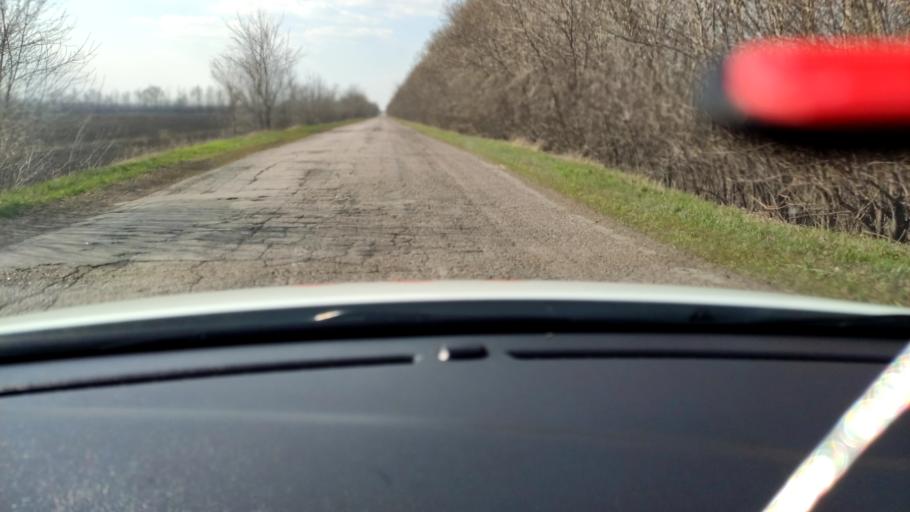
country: RU
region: Voronezj
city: Uryv-Pokrovka
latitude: 51.1323
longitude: 39.0966
